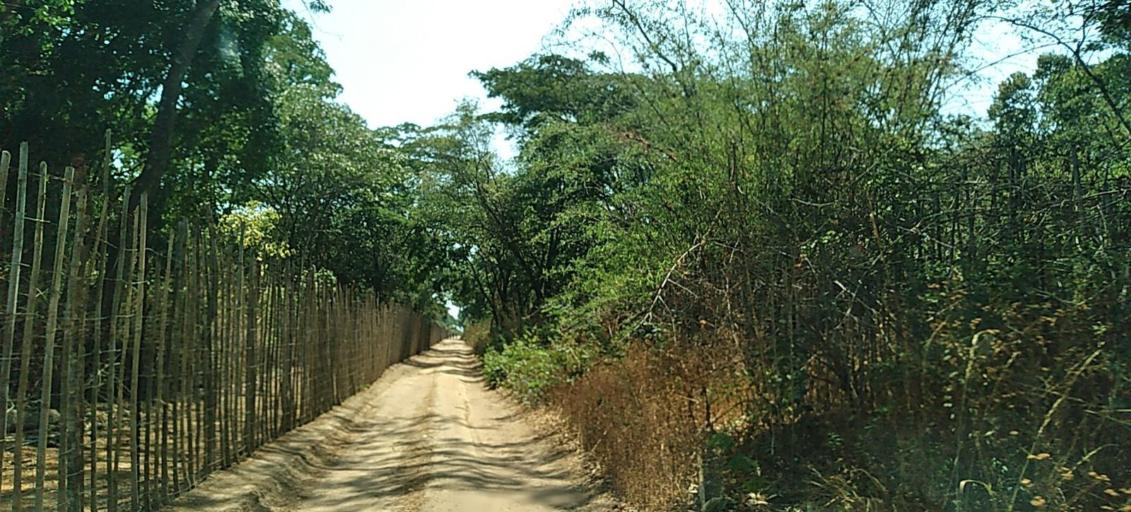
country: ZM
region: Copperbelt
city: Luanshya
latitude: -13.0097
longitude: 28.4667
